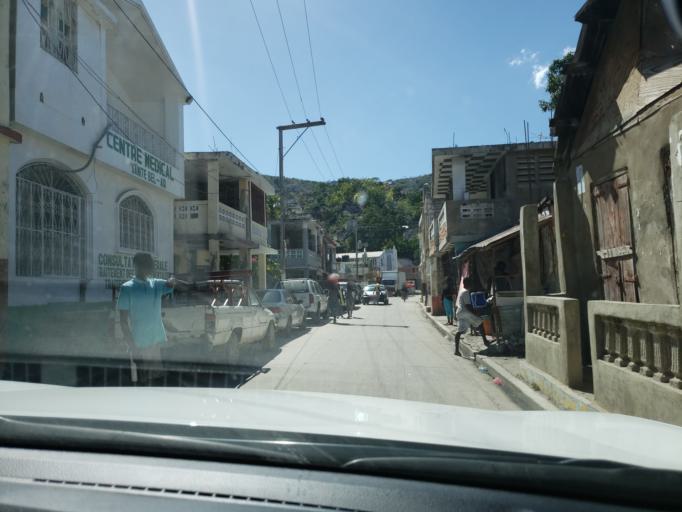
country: HT
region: Nippes
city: Miragoane
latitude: 18.4434
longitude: -73.0906
